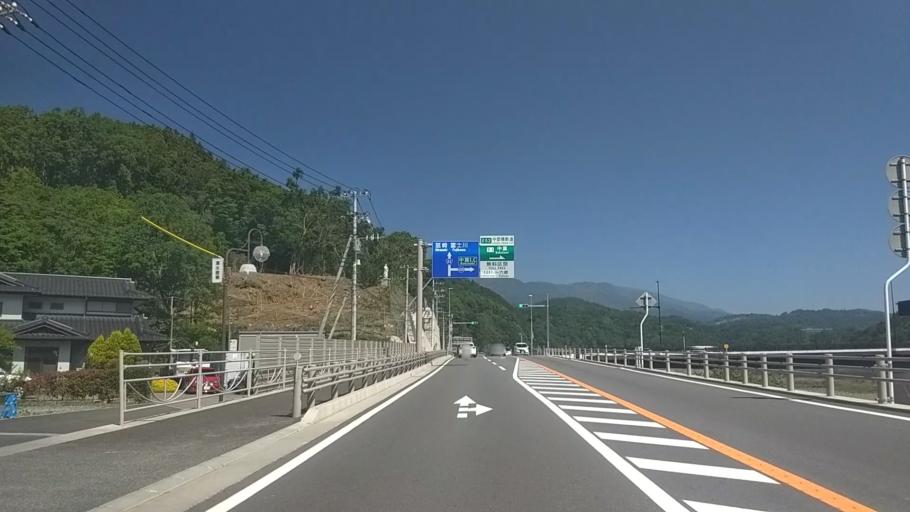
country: JP
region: Yamanashi
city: Ryuo
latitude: 35.4555
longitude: 138.4455
